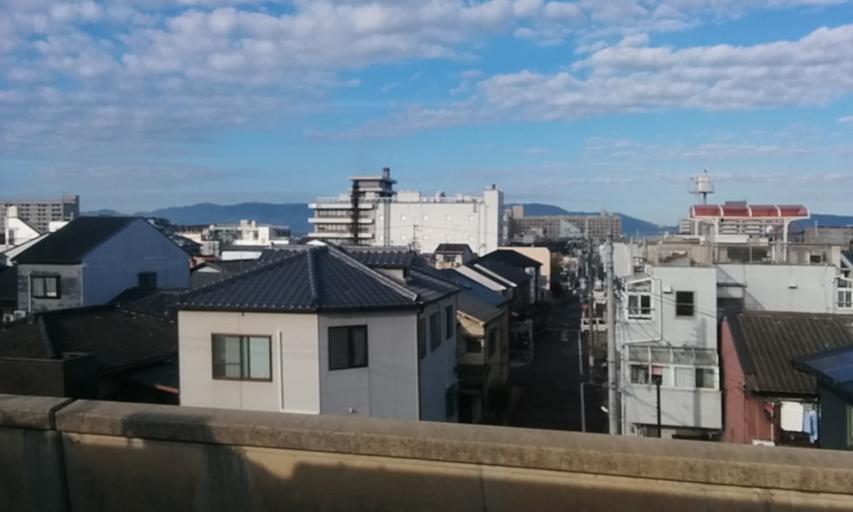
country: JP
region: Kyoto
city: Kyoto
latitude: 34.9768
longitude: 135.7525
